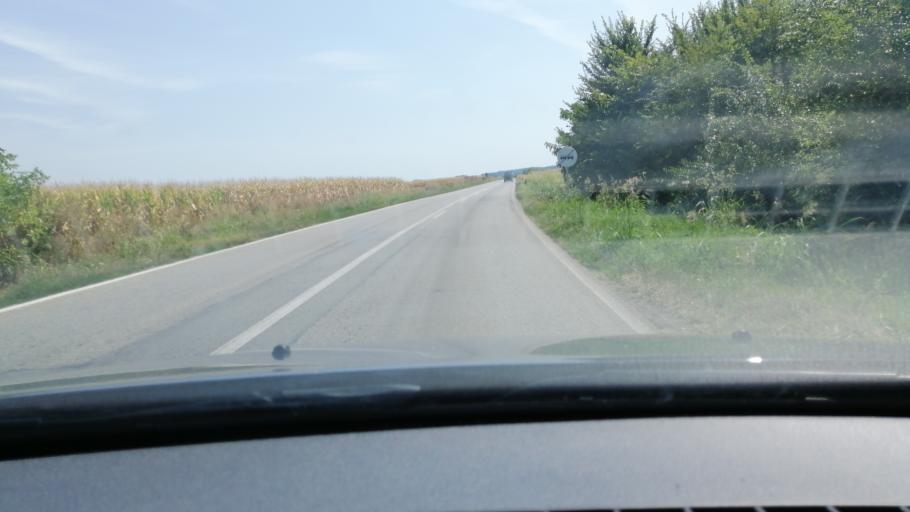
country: RS
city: Sutjeska
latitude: 45.3812
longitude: 20.7271
